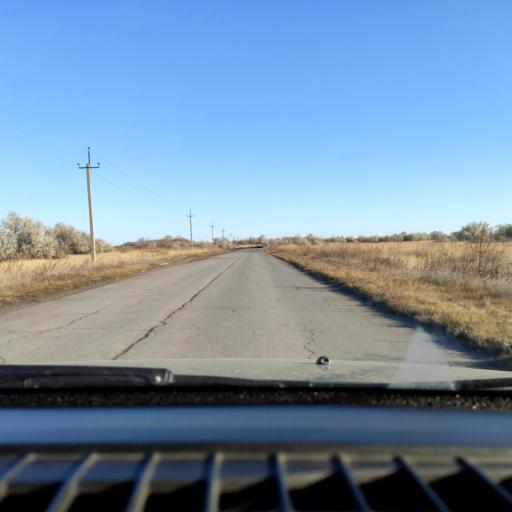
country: RU
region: Samara
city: Tol'yatti
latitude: 53.6541
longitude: 49.3274
